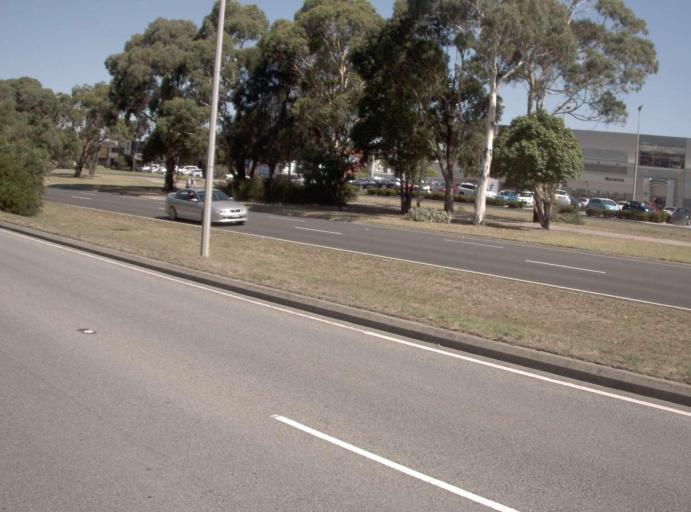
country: AU
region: Victoria
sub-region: Casey
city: Hallam
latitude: -38.0070
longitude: 145.2752
